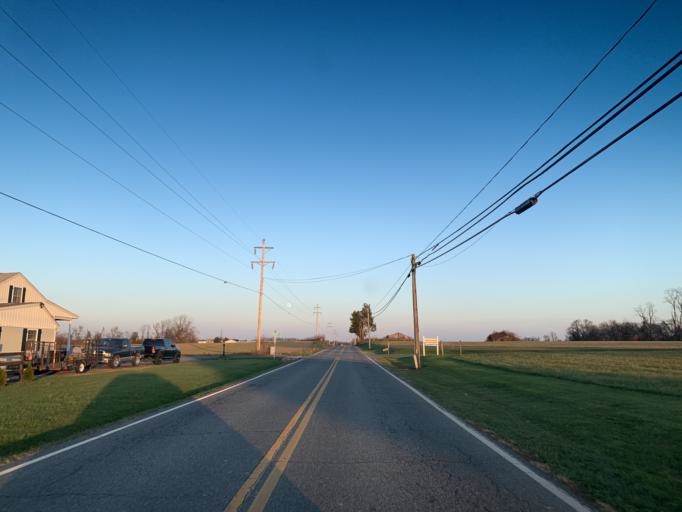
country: US
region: Maryland
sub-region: Cecil County
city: Charlestown
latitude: 39.4103
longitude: -75.9177
